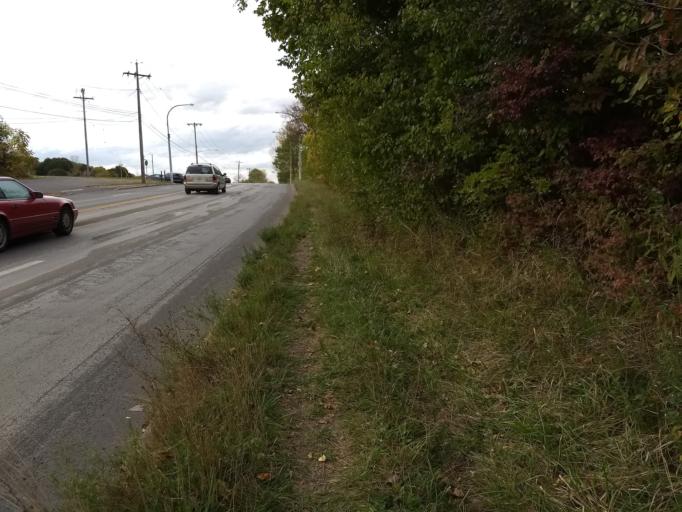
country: US
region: New York
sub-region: Onondaga County
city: Solvay
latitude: 43.0556
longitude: -76.1856
